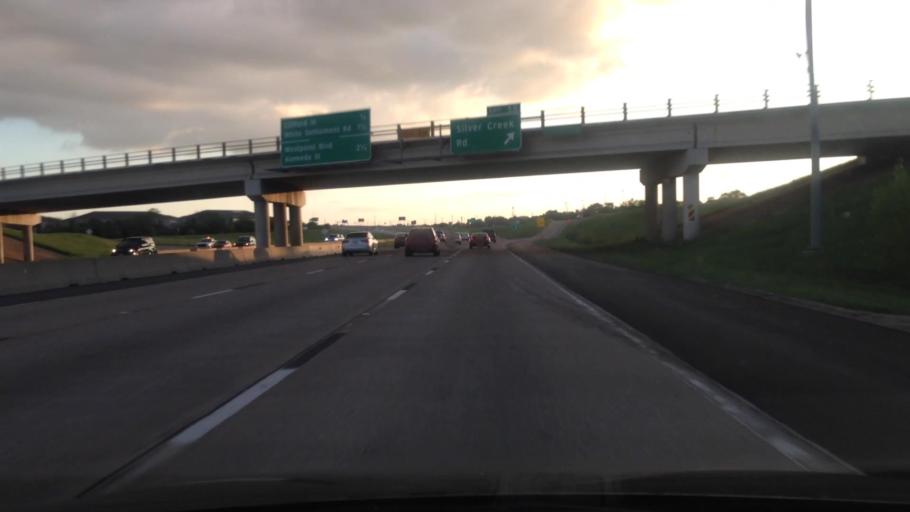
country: US
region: Texas
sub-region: Tarrant County
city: White Settlement
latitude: 32.7836
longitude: -97.4670
